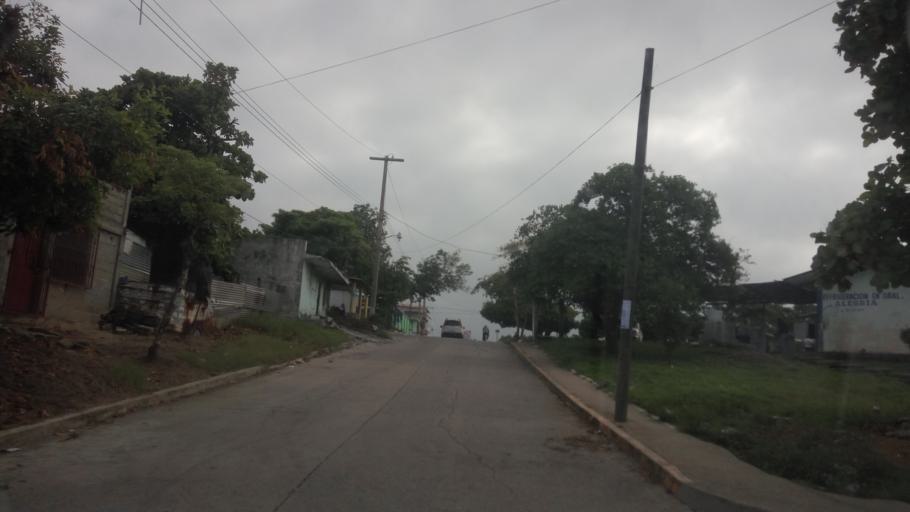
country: MX
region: Chiapas
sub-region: Reforma
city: El Carmen (El Limon)
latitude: 17.8562
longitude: -93.1546
